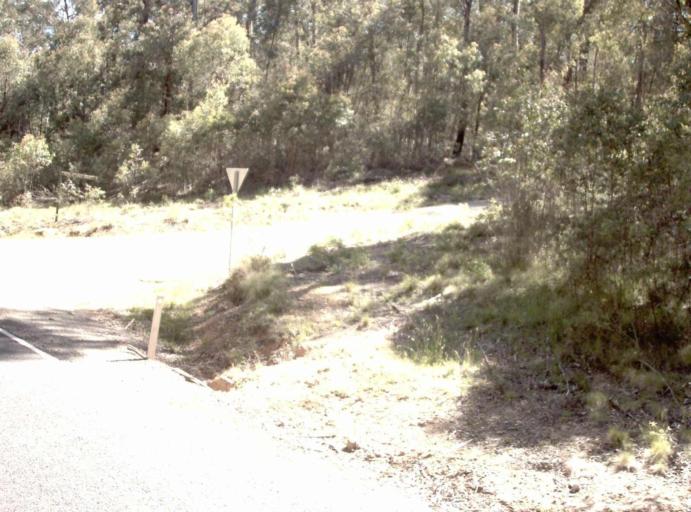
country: AU
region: New South Wales
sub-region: Bombala
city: Bombala
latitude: -37.1547
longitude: 148.7246
